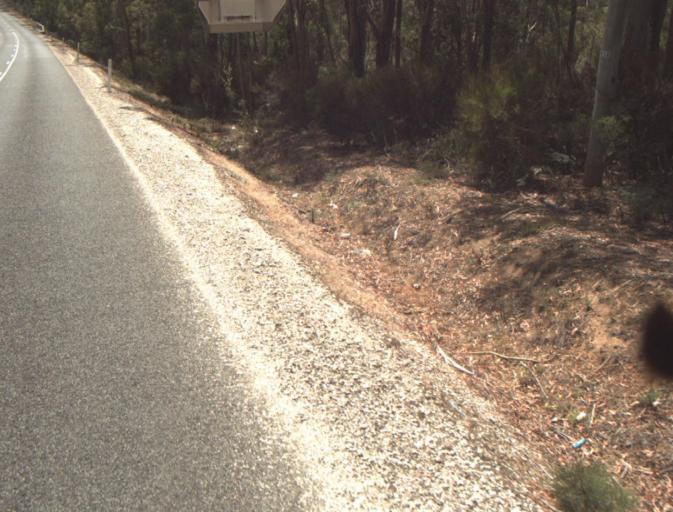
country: AU
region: Tasmania
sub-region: Launceston
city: Mayfield
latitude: -41.3001
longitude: 147.1334
